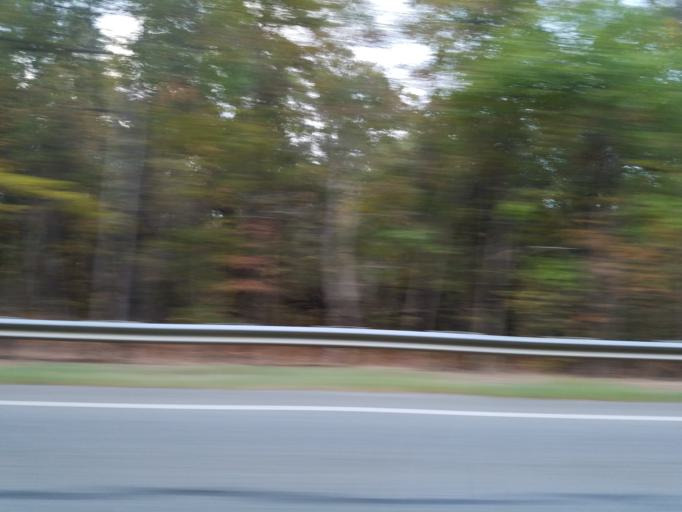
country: US
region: Georgia
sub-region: Murray County
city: Chatsworth
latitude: 34.5892
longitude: -84.6750
